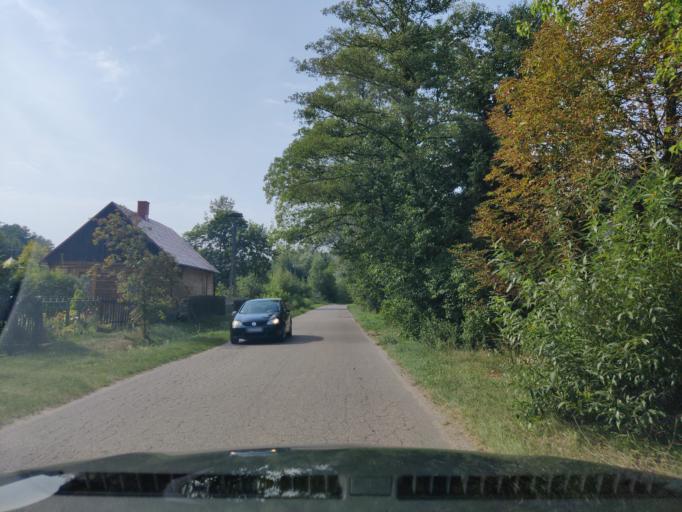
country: PL
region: Masovian Voivodeship
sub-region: Powiat wyszkowski
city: Rzasnik
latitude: 52.7431
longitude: 21.3200
